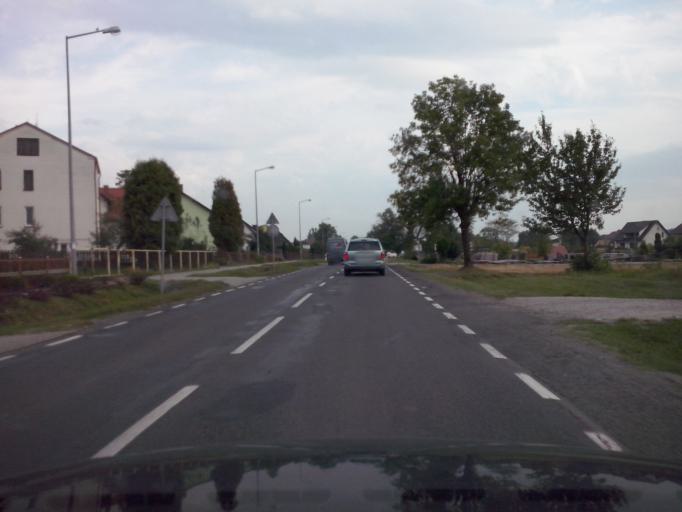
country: PL
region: Lublin Voivodeship
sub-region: Powiat bilgorajski
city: Bilgoraj
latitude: 50.5057
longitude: 22.7209
